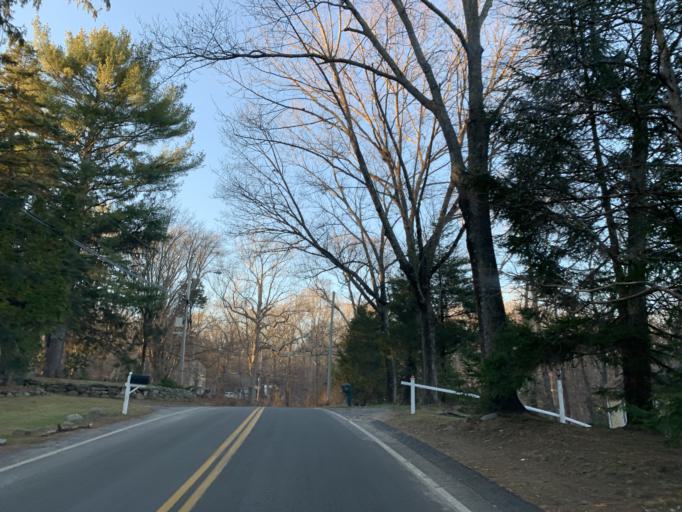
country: US
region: Rhode Island
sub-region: Kent County
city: East Greenwich
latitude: 41.6626
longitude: -71.4731
